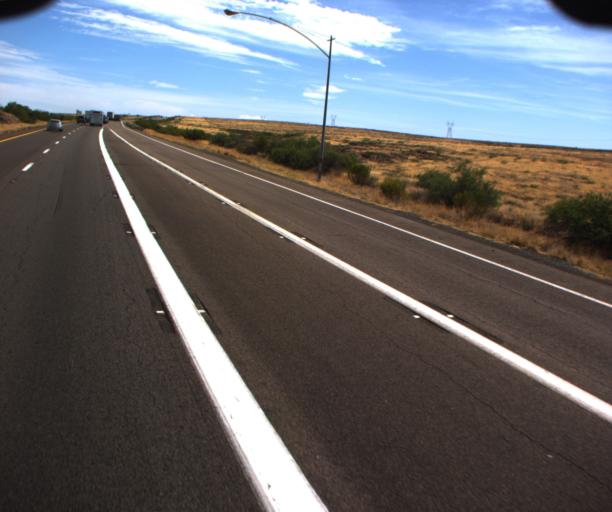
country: US
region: Arizona
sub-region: Yavapai County
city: Cordes Lakes
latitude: 34.1970
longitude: -112.1291
